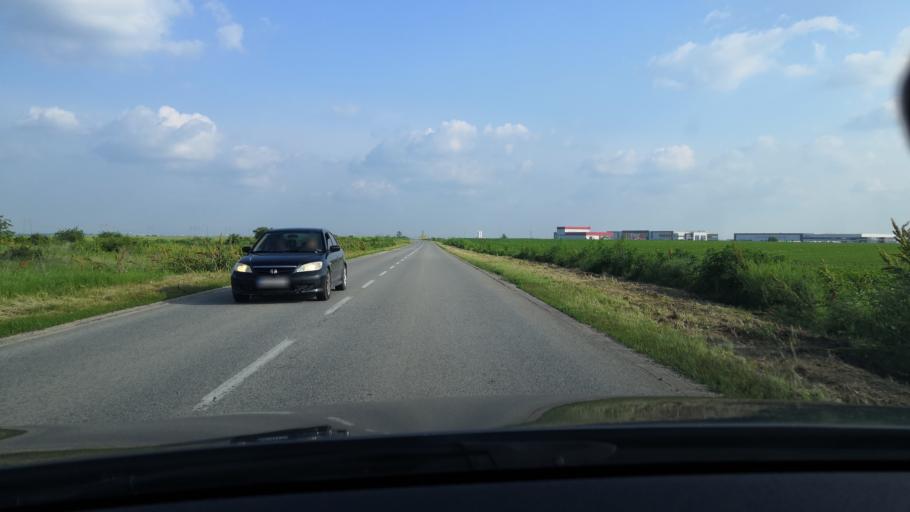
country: RS
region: Autonomna Pokrajina Vojvodina
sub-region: Sremski Okrug
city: Ingija
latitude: 45.0708
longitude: 20.1259
